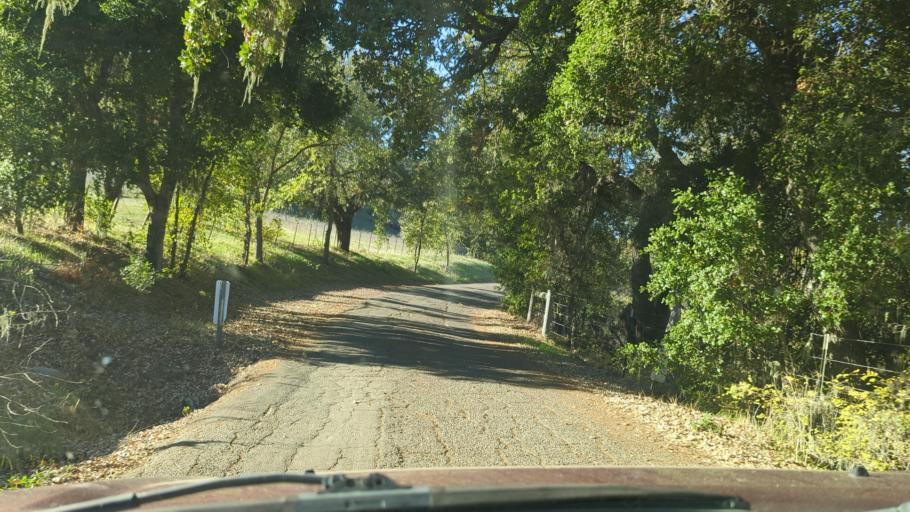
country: US
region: California
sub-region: Santa Barbara County
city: Santa Ynez
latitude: 34.5644
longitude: -120.0922
